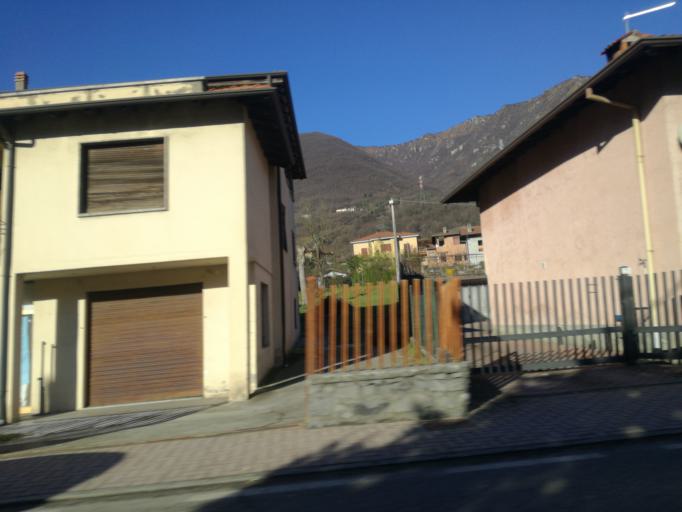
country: IT
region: Lombardy
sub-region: Provincia di Bergamo
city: Piangaiano
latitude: 45.7887
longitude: 10.0001
